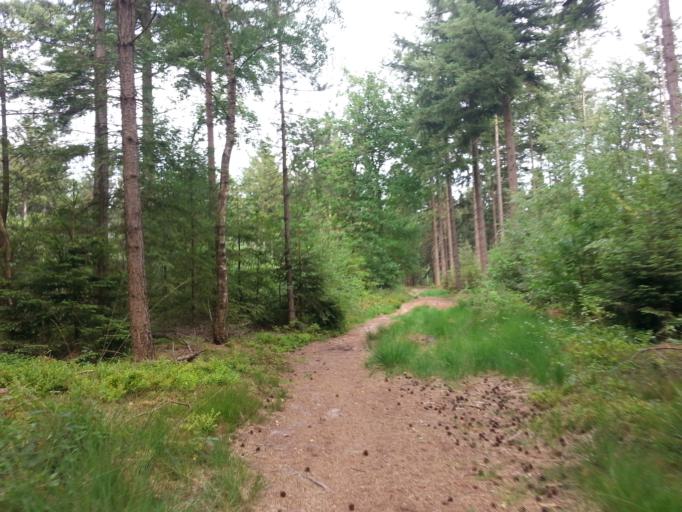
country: NL
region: Utrecht
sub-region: Gemeente Amersfoort
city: Randenbroek
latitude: 52.1108
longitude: 5.3813
